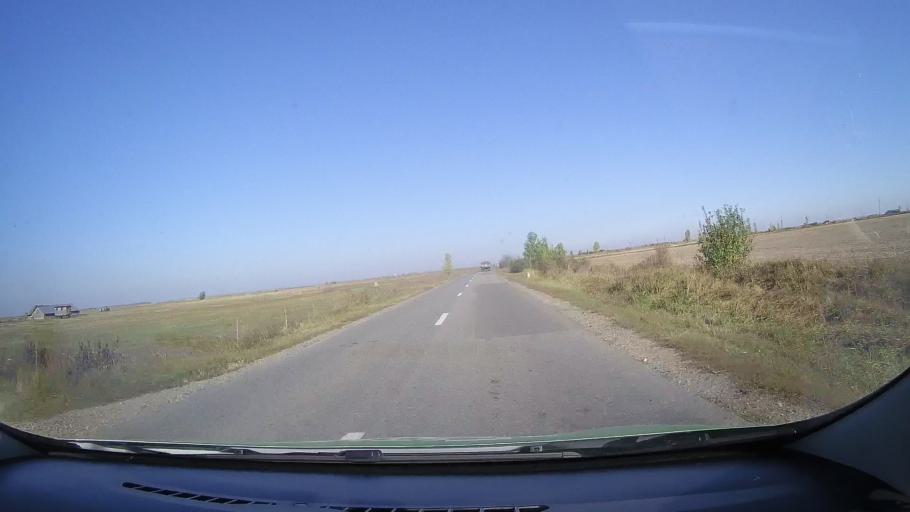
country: RO
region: Satu Mare
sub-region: Comuna Cauas
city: Cauas
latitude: 47.5331
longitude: 22.5659
